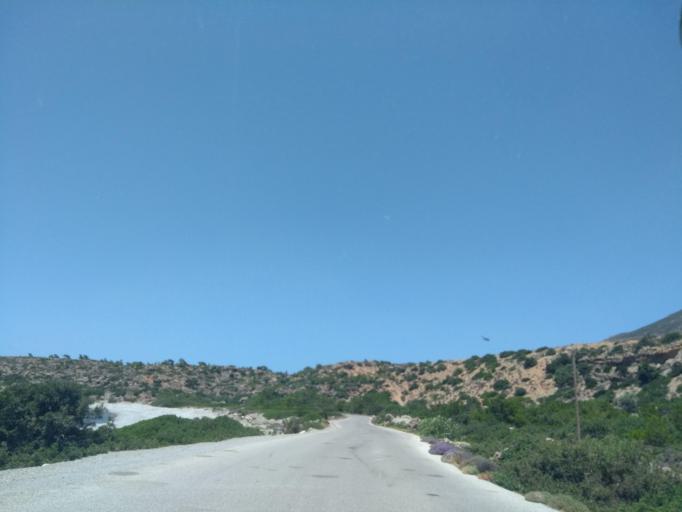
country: GR
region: Crete
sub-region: Nomos Chanias
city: Vryses
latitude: 35.3278
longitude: 23.5489
